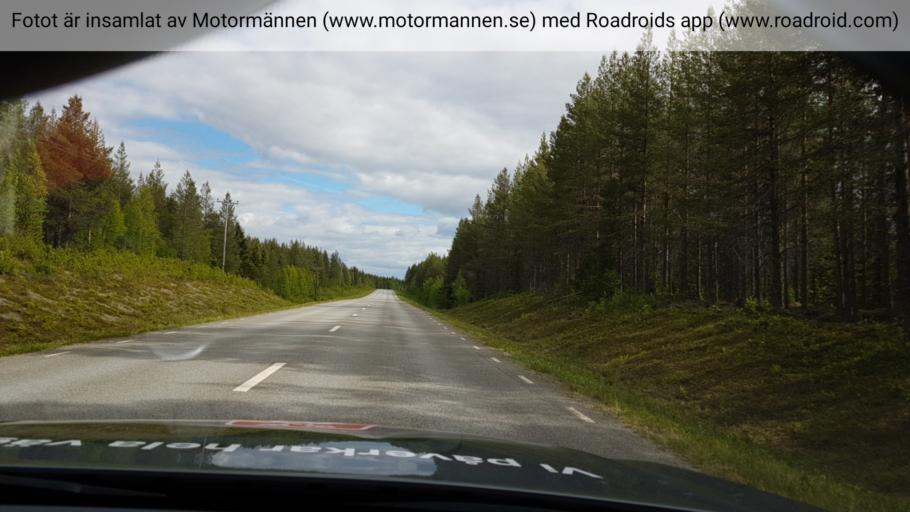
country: SE
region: Jaemtland
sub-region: Stroemsunds Kommun
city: Stroemsund
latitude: 64.2809
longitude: 15.3624
